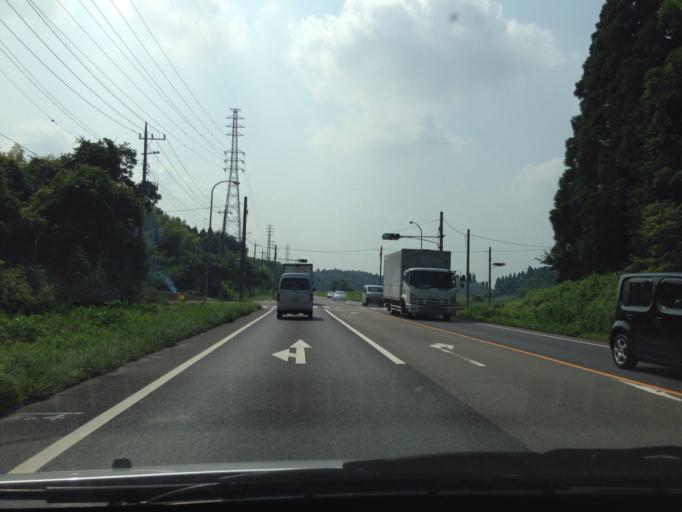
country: JP
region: Ibaraki
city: Ami
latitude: 36.0273
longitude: 140.2334
